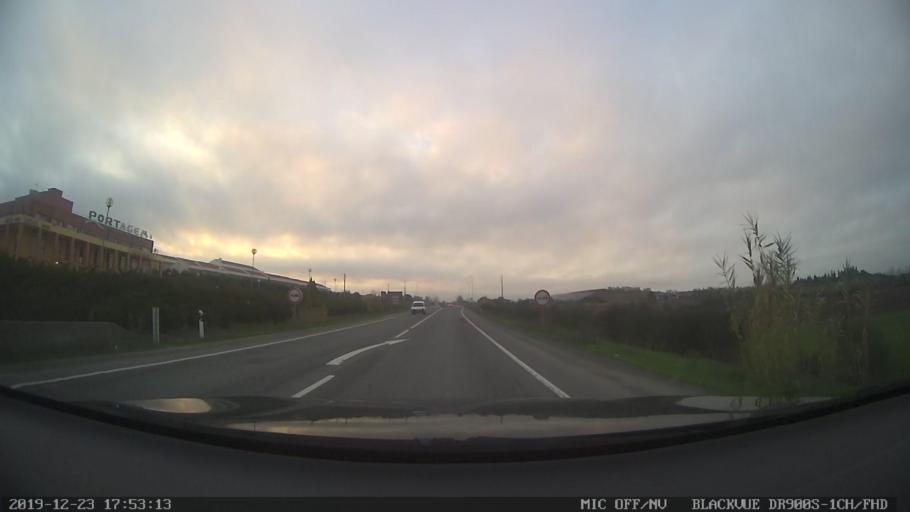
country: PT
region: Aveiro
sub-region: Mealhada
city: Mealhada
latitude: 40.3726
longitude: -8.4797
